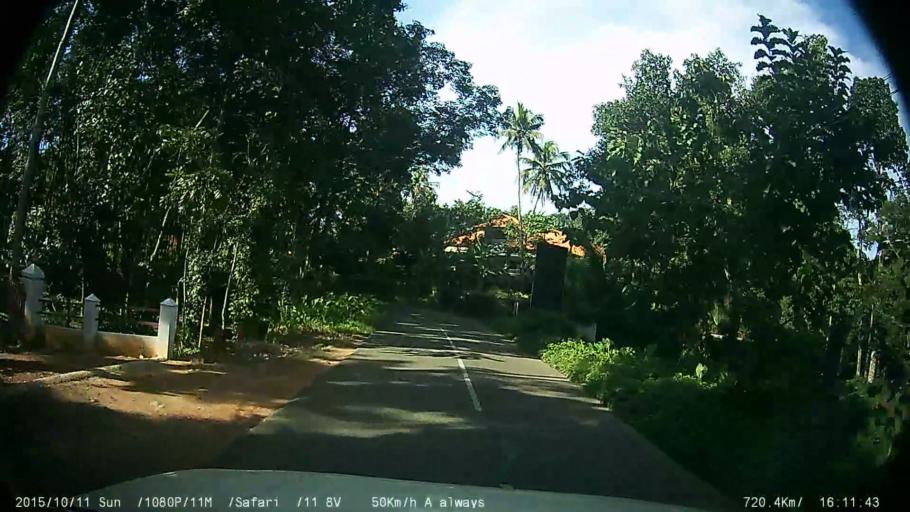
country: IN
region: Kerala
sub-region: Kottayam
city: Palackattumala
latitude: 9.7106
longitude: 76.6099
